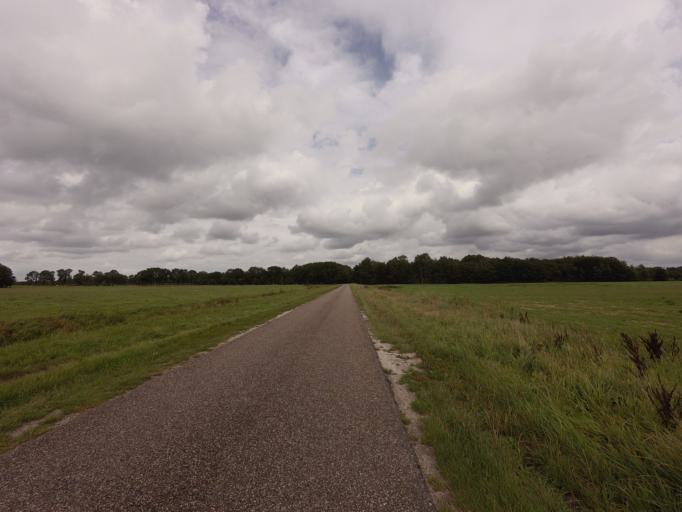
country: NL
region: Friesland
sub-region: Gemeente Weststellingwerf
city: Noordwolde
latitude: 52.9308
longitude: 6.1584
